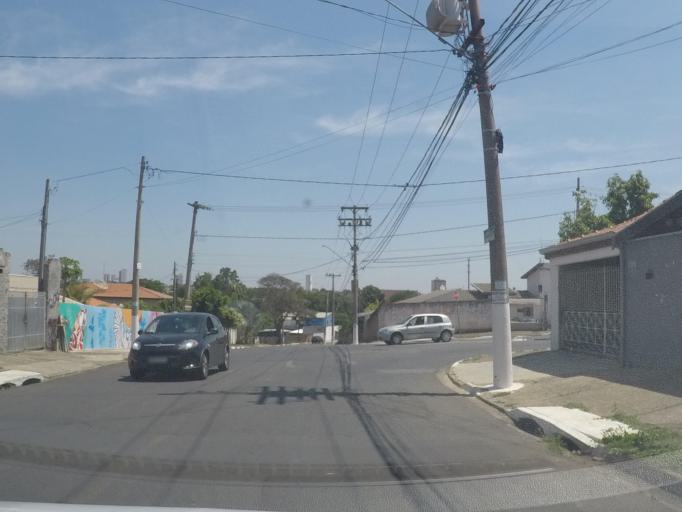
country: BR
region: Sao Paulo
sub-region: Hortolandia
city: Hortolandia
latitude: -22.8590
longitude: -47.2122
